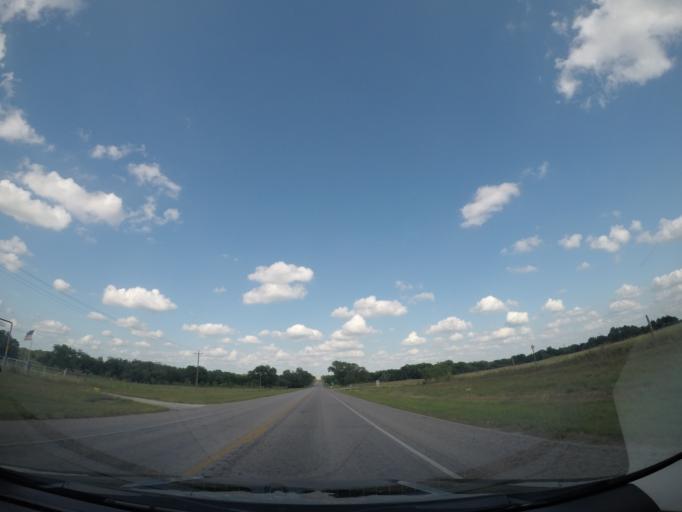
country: US
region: Texas
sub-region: Lavaca County
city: Shiner
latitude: 29.4294
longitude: -97.0869
